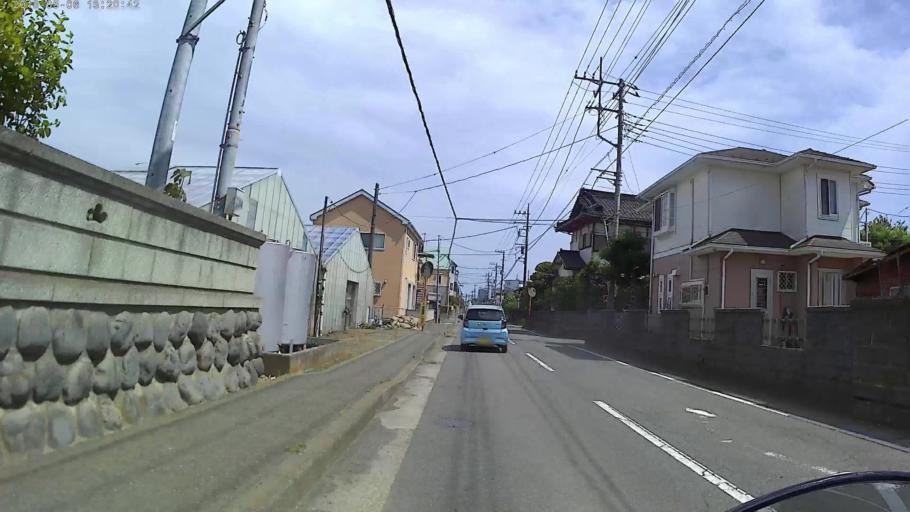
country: JP
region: Kanagawa
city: Fujisawa
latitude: 35.4105
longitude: 139.4461
